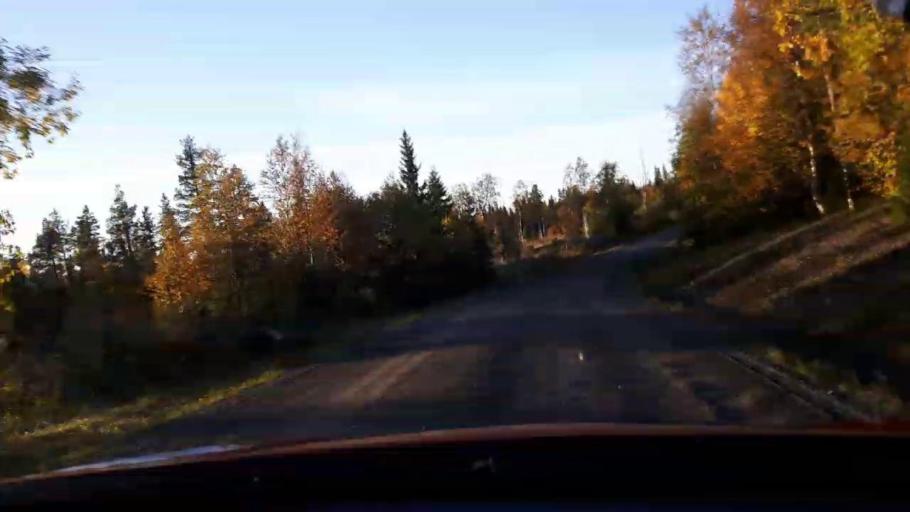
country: SE
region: Jaemtland
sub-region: Krokoms Kommun
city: Krokom
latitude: 63.4182
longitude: 14.6082
